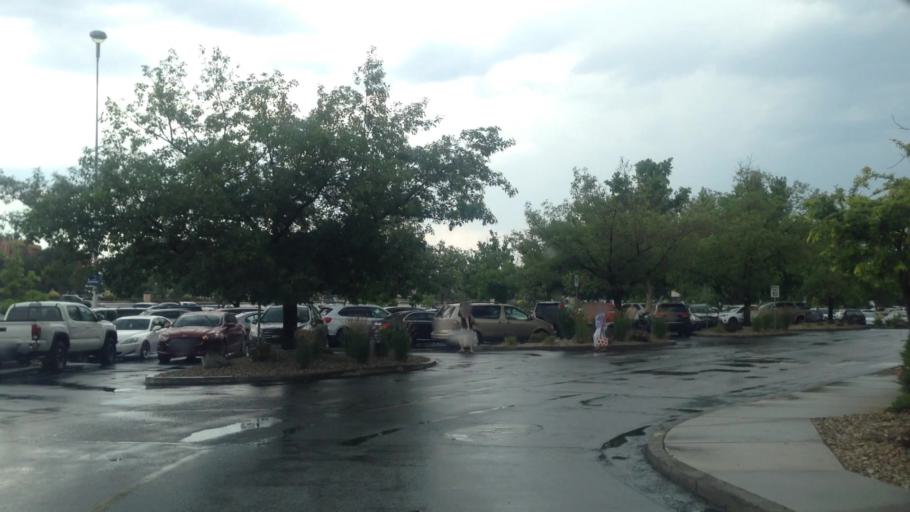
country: US
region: Nevada
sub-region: Washoe County
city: Reno
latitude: 39.4741
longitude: -119.7843
